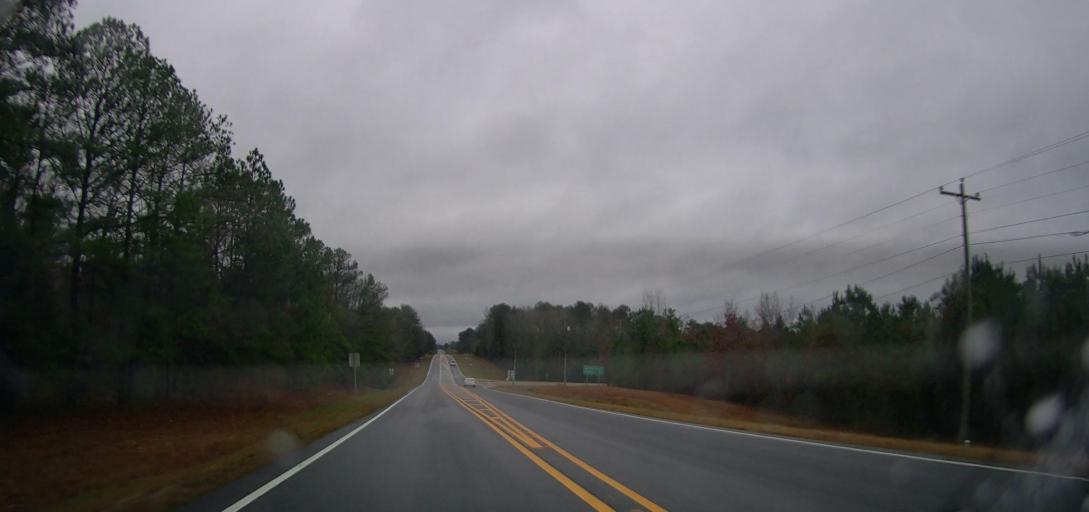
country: US
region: Alabama
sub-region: Bibb County
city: Centreville
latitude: 32.8148
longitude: -86.9339
